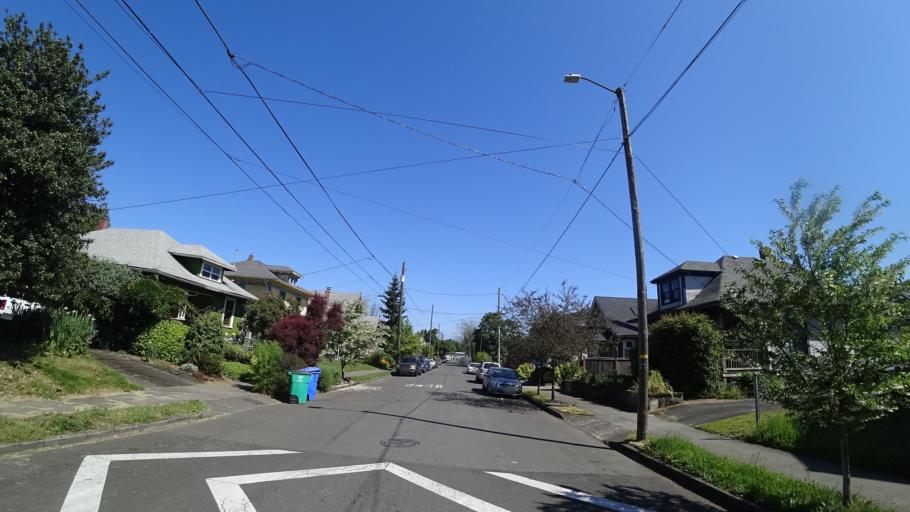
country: US
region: Oregon
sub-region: Multnomah County
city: Portland
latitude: 45.5609
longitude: -122.6507
